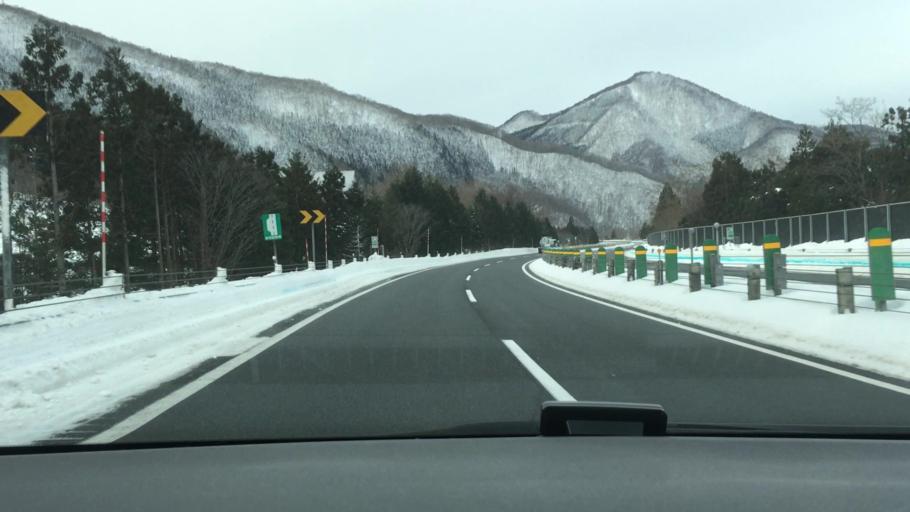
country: JP
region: Akita
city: Hanawa
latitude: 40.1351
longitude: 140.9537
